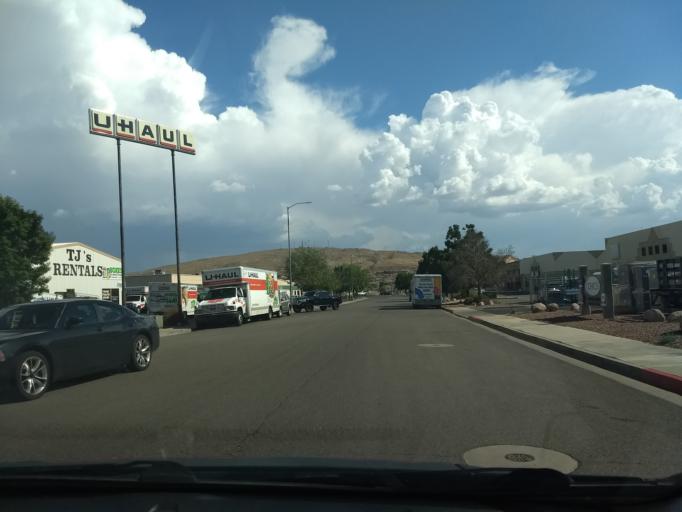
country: US
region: Utah
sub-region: Washington County
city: Saint George
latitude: 37.0837
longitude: -113.5782
